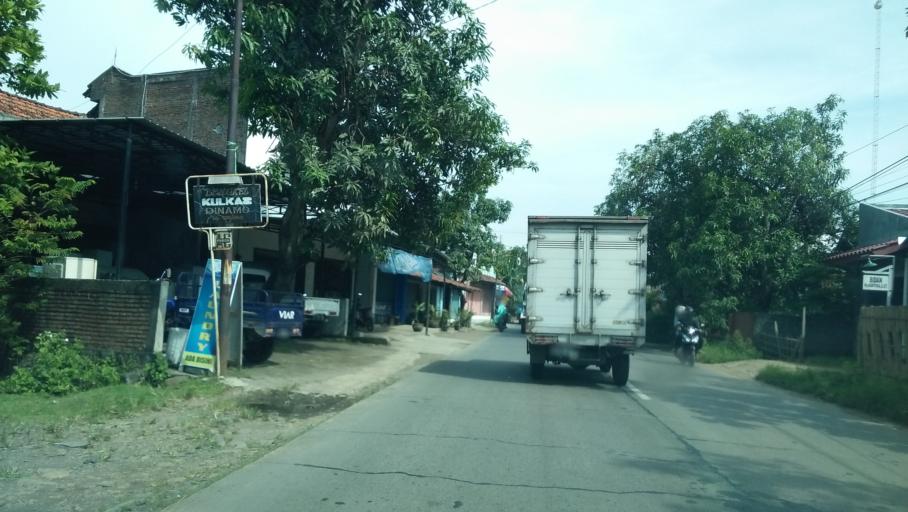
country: ID
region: Central Java
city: Welahan
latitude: -6.7934
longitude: 110.7252
